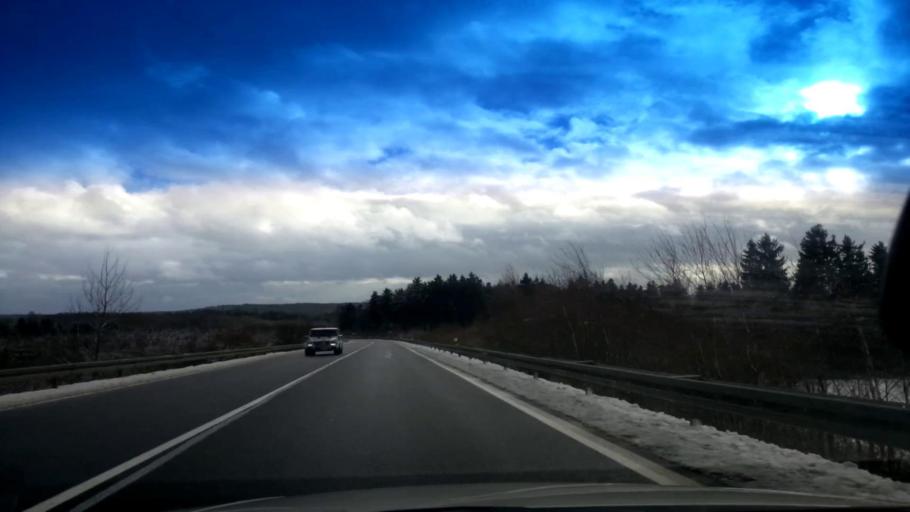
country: CZ
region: Karlovarsky
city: As
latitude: 50.2118
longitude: 12.1801
